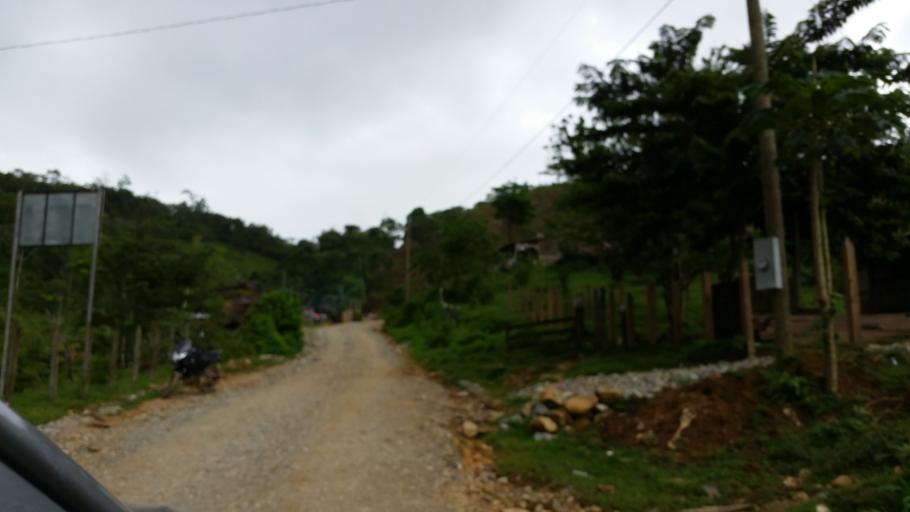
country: NI
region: Atlantico Norte (RAAN)
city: Bonanza
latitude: 13.9756
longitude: -84.6953
